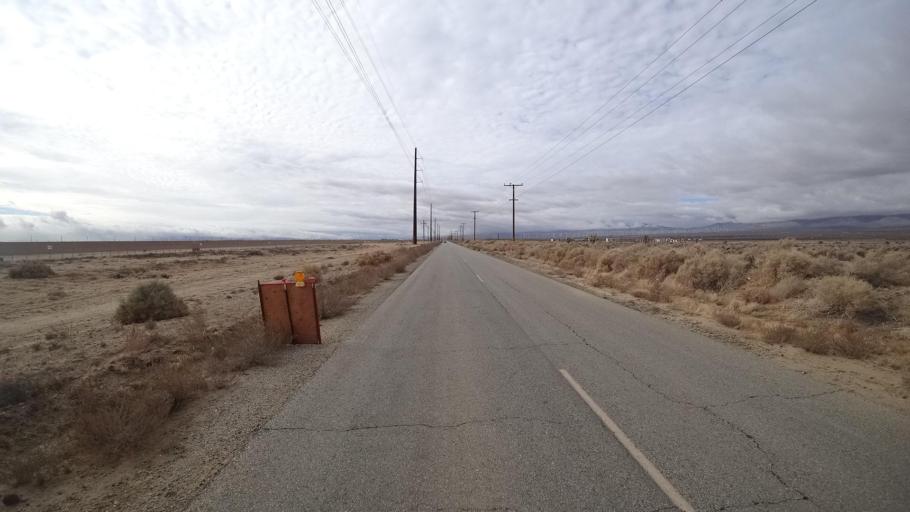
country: US
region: California
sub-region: Kern County
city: Rosamond
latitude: 34.8633
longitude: -118.3329
